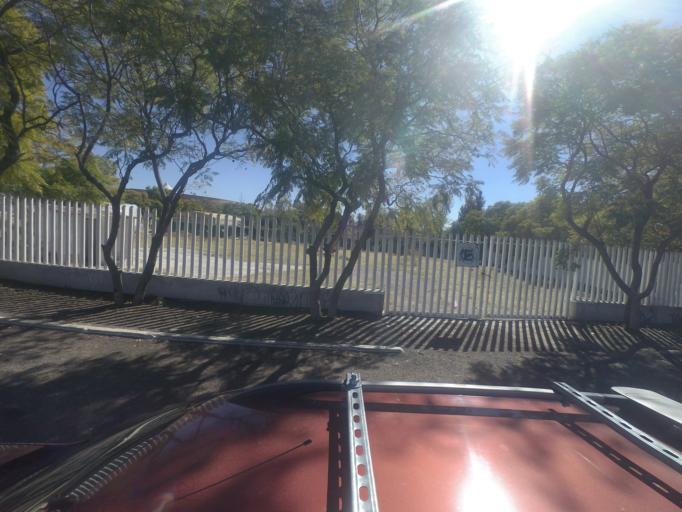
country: MX
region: Aguascalientes
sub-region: Aguascalientes
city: Aguascalientes
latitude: 21.8576
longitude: -102.2910
